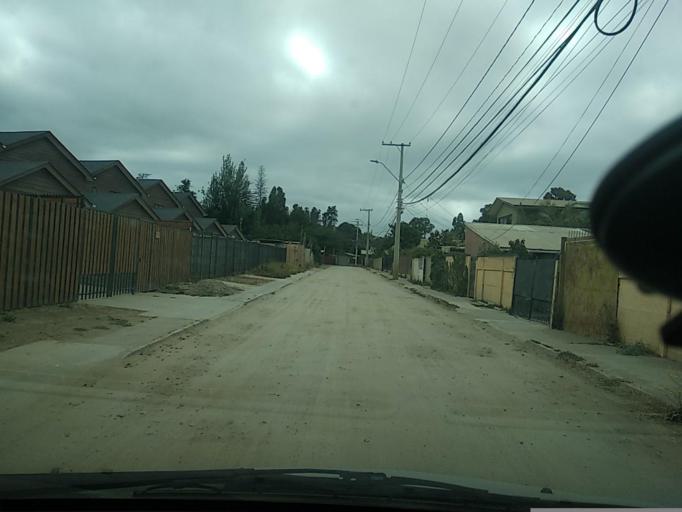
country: CL
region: Valparaiso
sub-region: Provincia de Marga Marga
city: Villa Alemana
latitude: -33.0383
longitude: -71.3599
